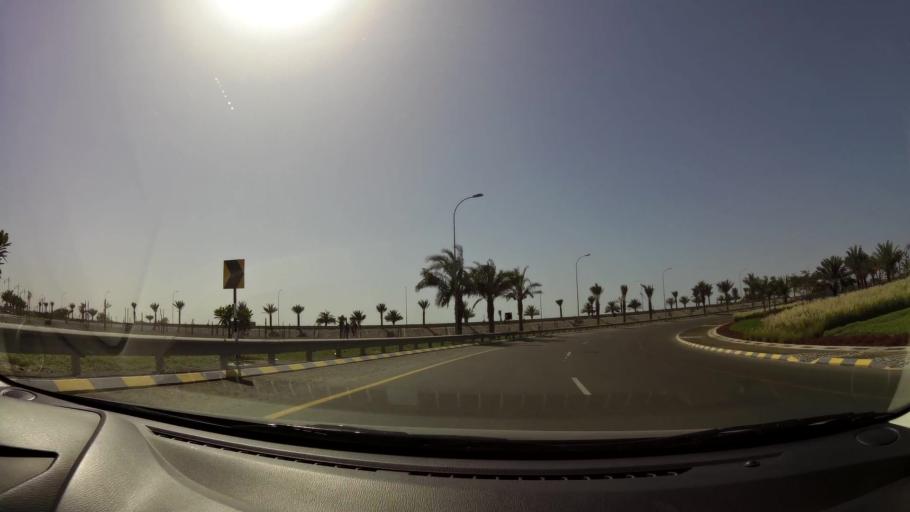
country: OM
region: Muhafazat Masqat
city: Bawshar
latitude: 23.5934
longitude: 58.3297
